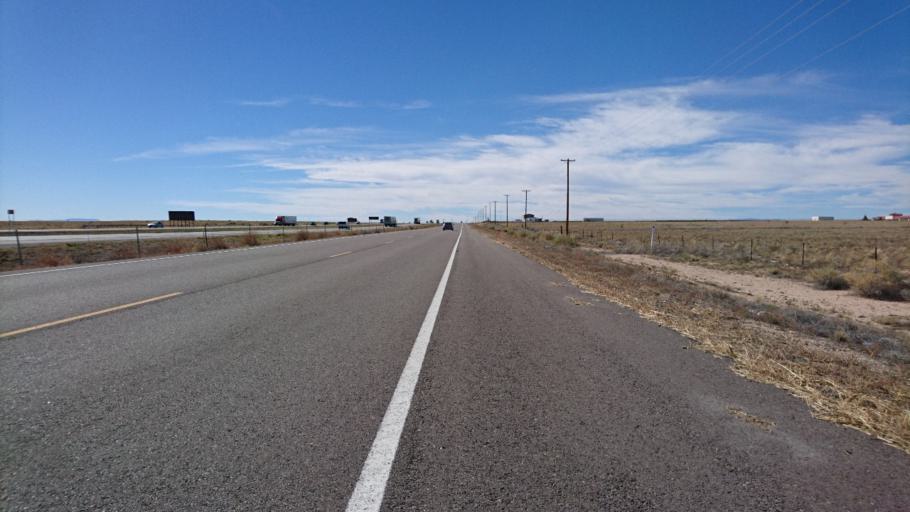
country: US
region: New Mexico
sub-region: Bernalillo County
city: South Valley
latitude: 35.0584
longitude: -106.8176
